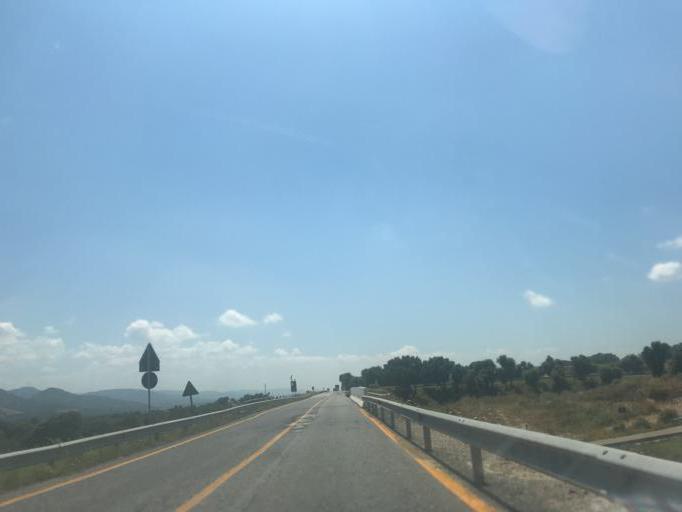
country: IT
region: Sardinia
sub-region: Provincia di Olbia-Tempio
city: Monti
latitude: 40.8029
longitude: 9.2805
